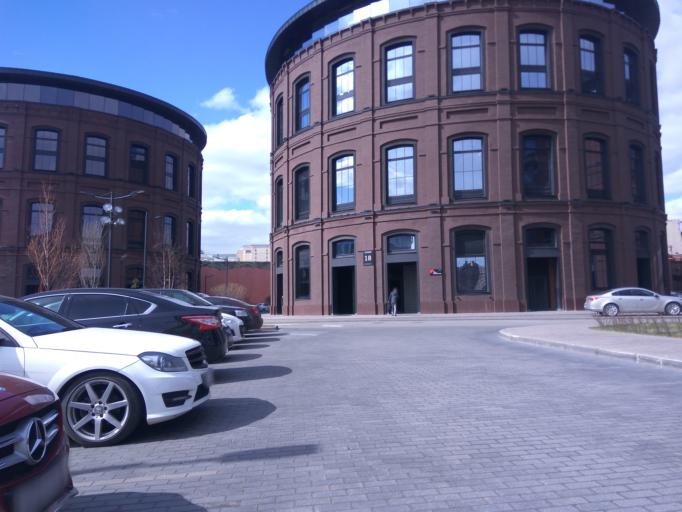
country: RU
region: Moscow
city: Taganskiy
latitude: 55.7590
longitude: 37.6654
